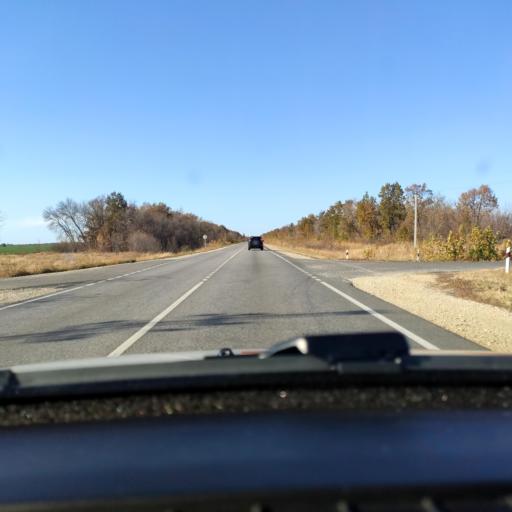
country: RU
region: Voronezj
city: Zemlyansk
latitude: 51.8253
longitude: 38.8340
